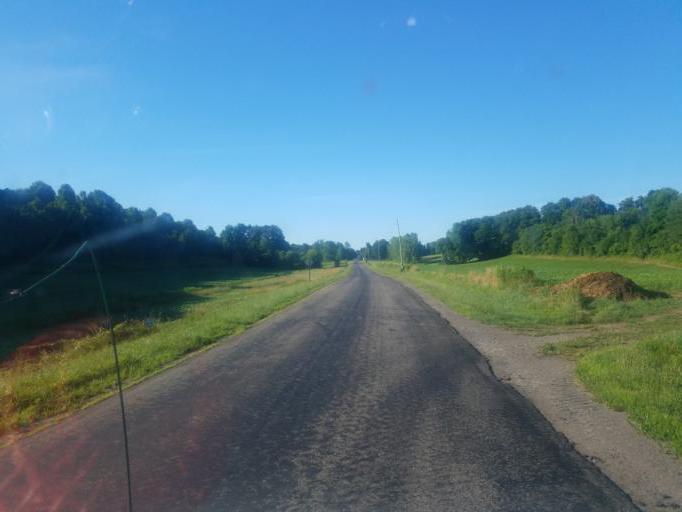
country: US
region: New York
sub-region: Wayne County
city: Lyons
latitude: 43.1100
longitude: -77.0460
